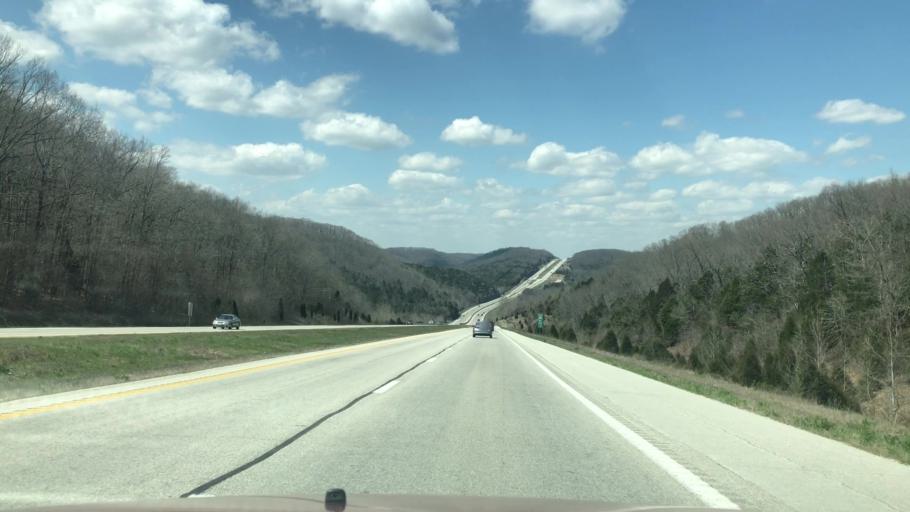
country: US
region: Missouri
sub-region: Taney County
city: Merriam Woods
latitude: 36.8507
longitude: -93.2224
